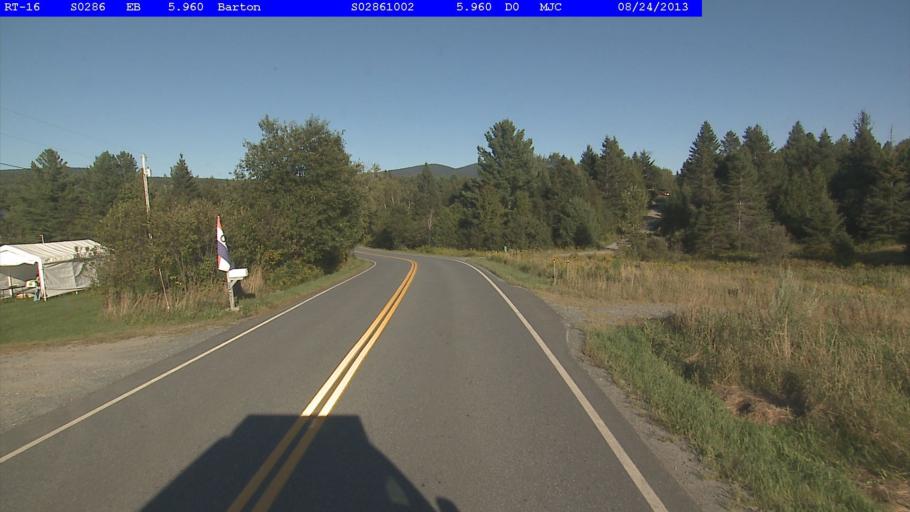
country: US
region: Vermont
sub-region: Orleans County
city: Newport
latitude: 44.7823
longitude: -72.0894
